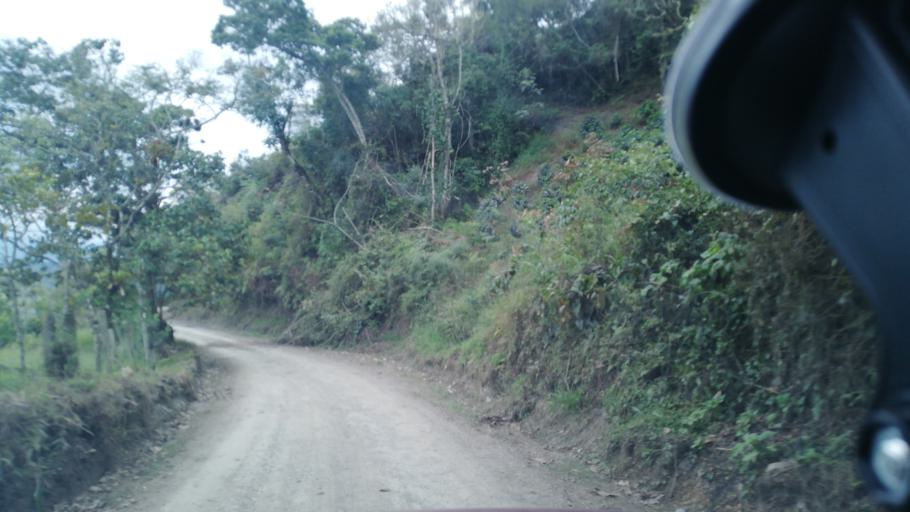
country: CO
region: Cundinamarca
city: Vergara
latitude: 5.1594
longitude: -74.2572
